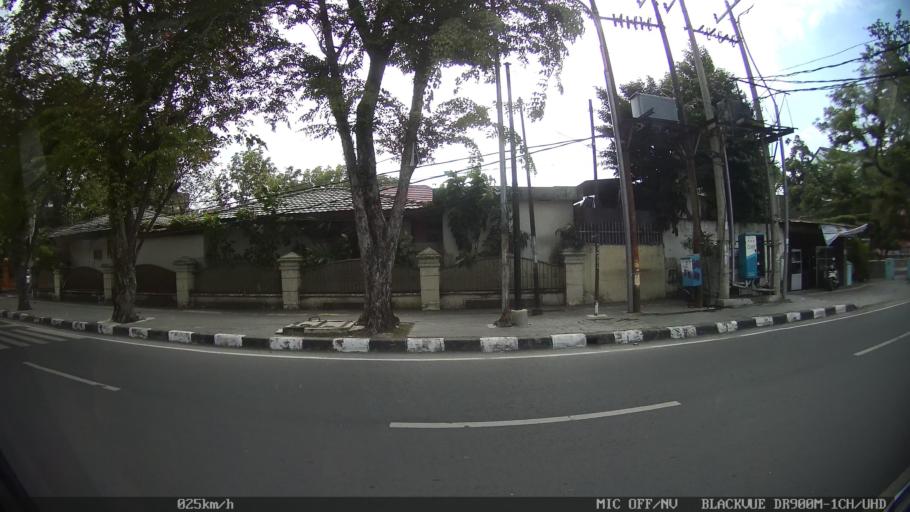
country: ID
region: North Sumatra
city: Medan
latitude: 3.5830
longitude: 98.6670
